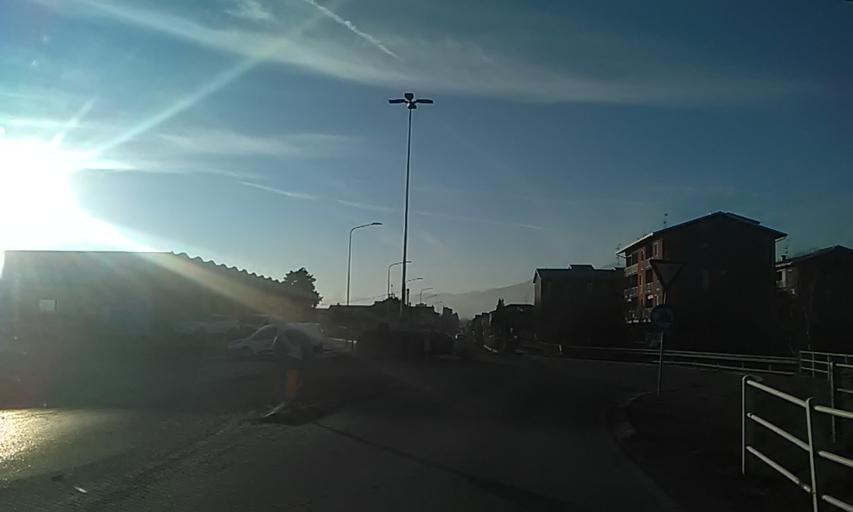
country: IT
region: Piedmont
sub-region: Provincia di Biella
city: Cerreto Castello
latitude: 45.5644
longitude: 8.1558
